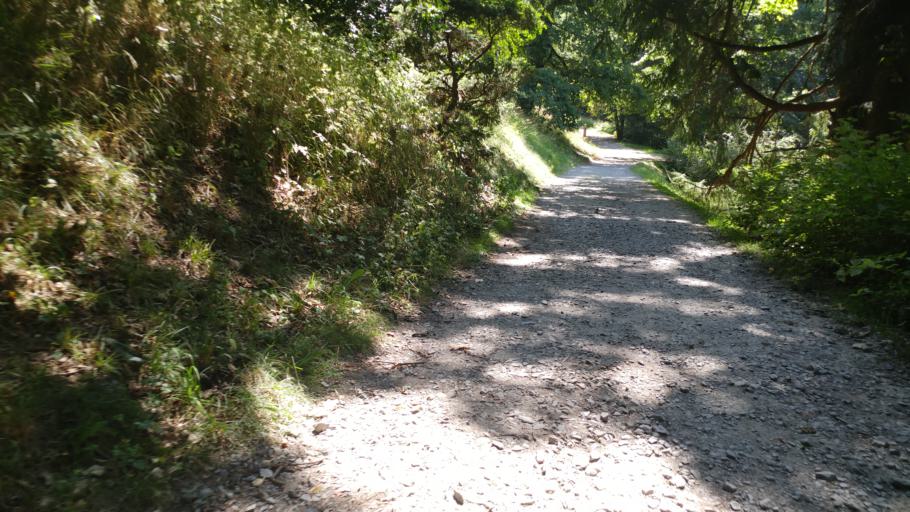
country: CZ
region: Central Bohemia
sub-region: Okres Praha-Zapad
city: Pruhonice
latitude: 49.9945
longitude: 14.5601
